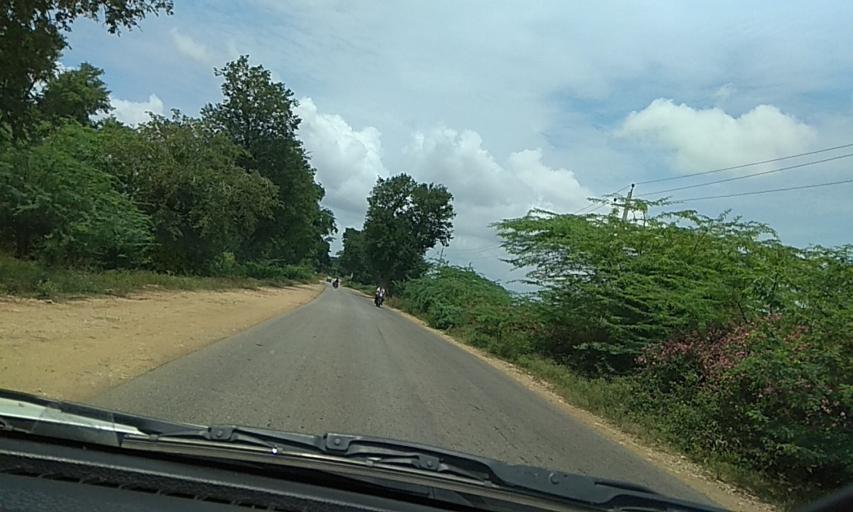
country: IN
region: Karnataka
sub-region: Chamrajnagar
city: Gundlupet
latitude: 11.8106
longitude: 76.7244
